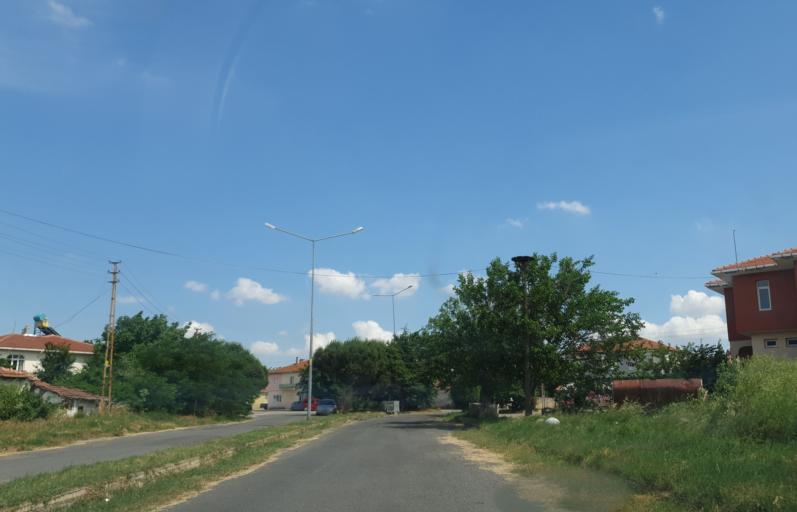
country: TR
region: Tekirdag
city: Muratli
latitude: 41.2175
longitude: 27.5452
